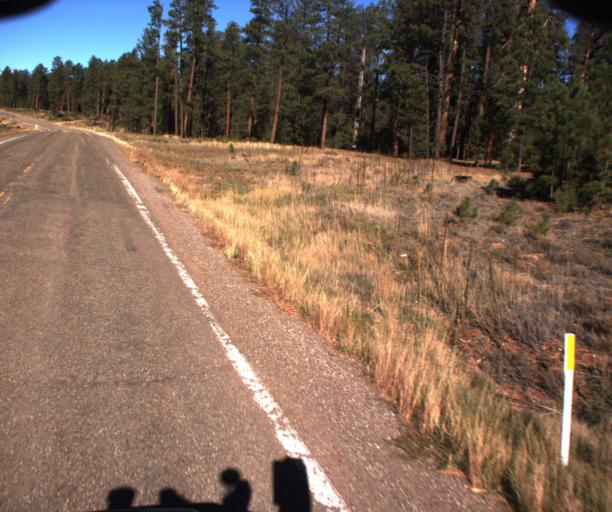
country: US
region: Arizona
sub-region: Coconino County
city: Fredonia
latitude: 36.7467
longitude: -112.2466
